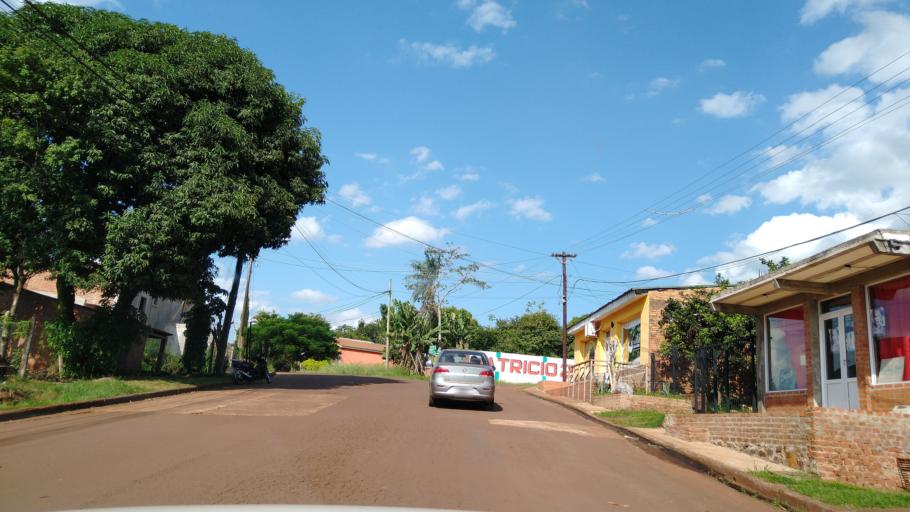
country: AR
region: Misiones
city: Puerto Piray
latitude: -26.4686
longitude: -54.7093
